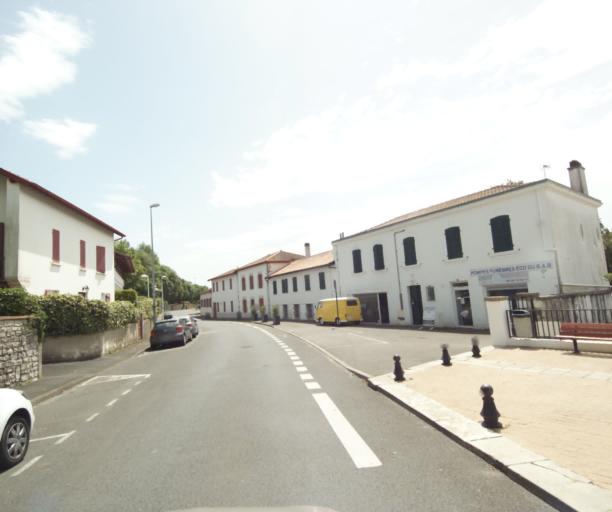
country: FR
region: Aquitaine
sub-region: Departement des Pyrenees-Atlantiques
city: Bayonne
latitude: 43.4798
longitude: -1.4597
